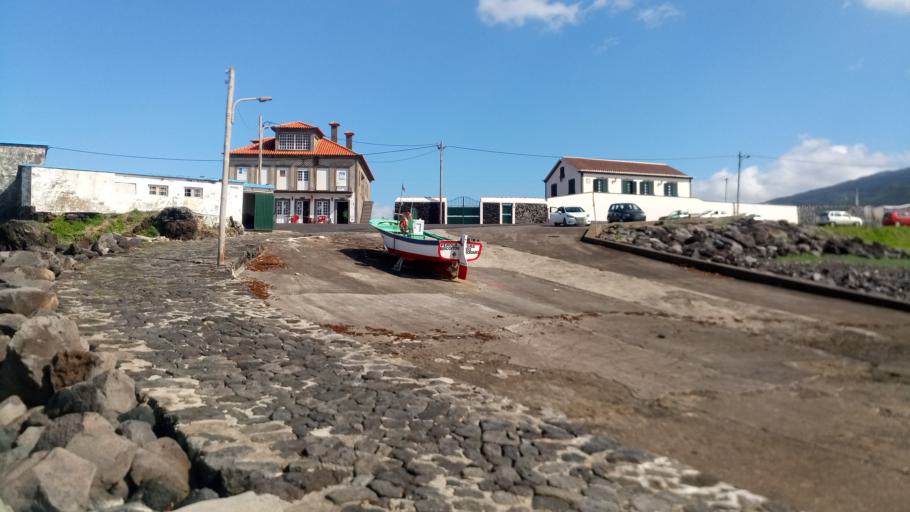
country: PT
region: Azores
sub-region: Praia da Vitoria
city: Biscoitos
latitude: 38.8008
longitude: -27.2590
